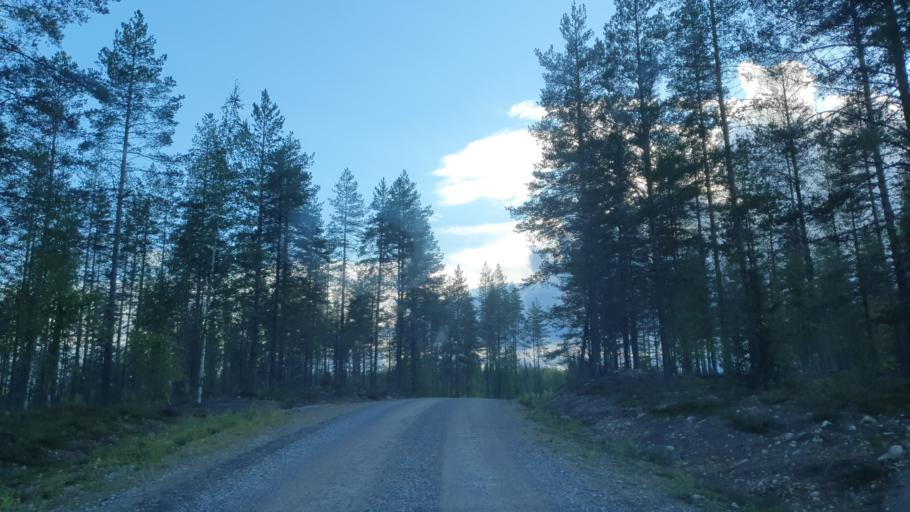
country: FI
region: Kainuu
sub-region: Kehys-Kainuu
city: Kuhmo
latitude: 64.3359
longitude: 29.9444
